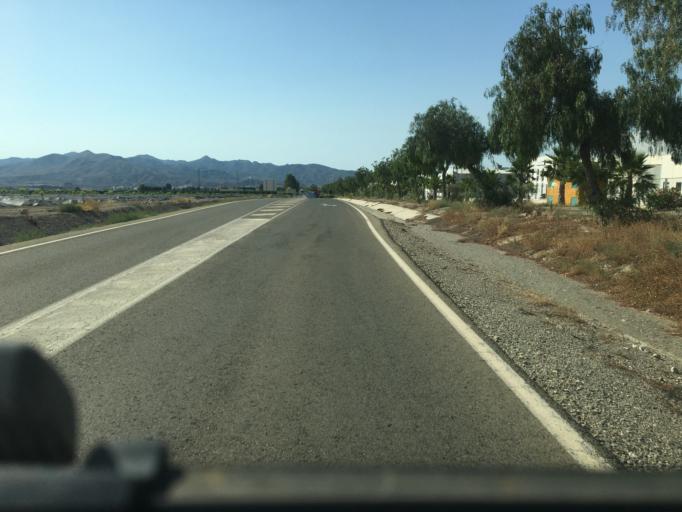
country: ES
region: Andalusia
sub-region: Provincia de Almeria
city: Huercal-Overa
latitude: 37.4177
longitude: -1.9676
